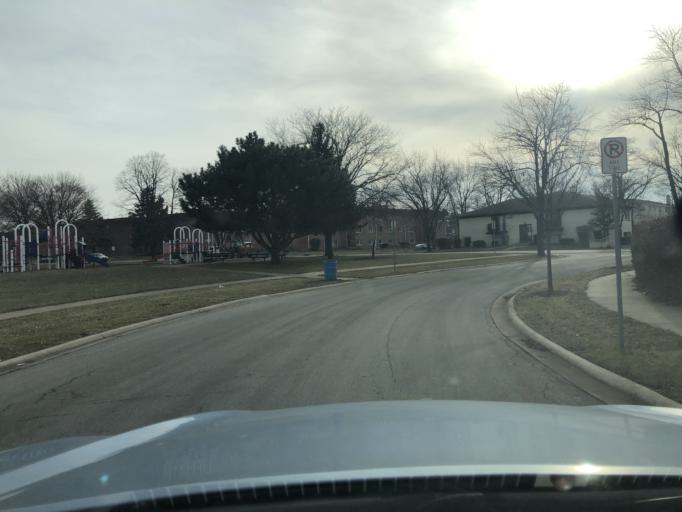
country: US
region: Illinois
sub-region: DuPage County
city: Addison
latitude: 41.9261
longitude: -87.9942
